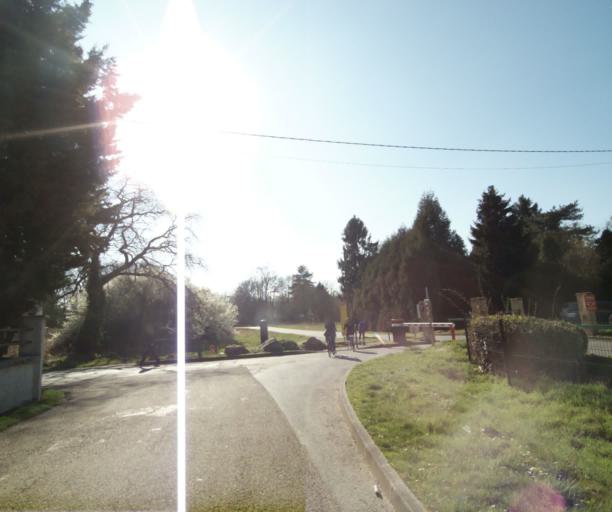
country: FR
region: Ile-de-France
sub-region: Departement du Val-d'Oise
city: Neuville-sur-Oise
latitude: 49.0275
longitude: 2.0549
